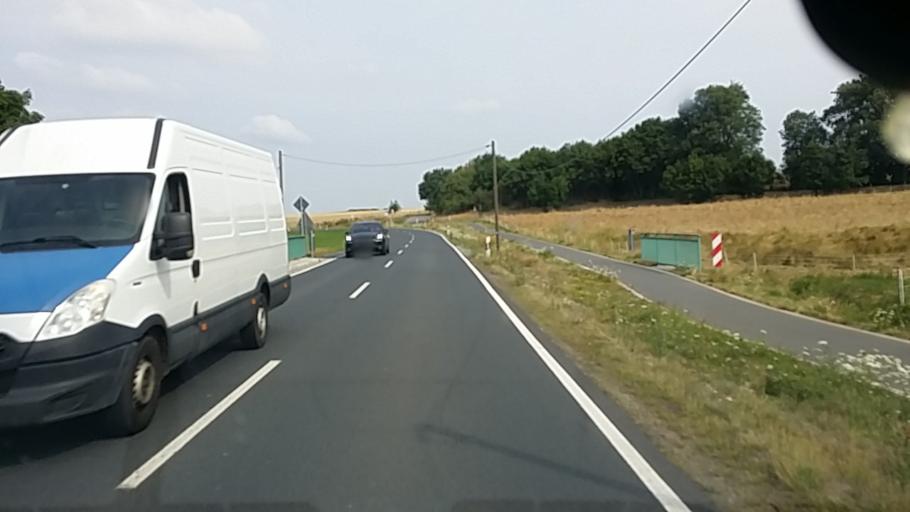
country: DE
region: Saxony
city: Wachau
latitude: 51.1637
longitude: 13.8747
